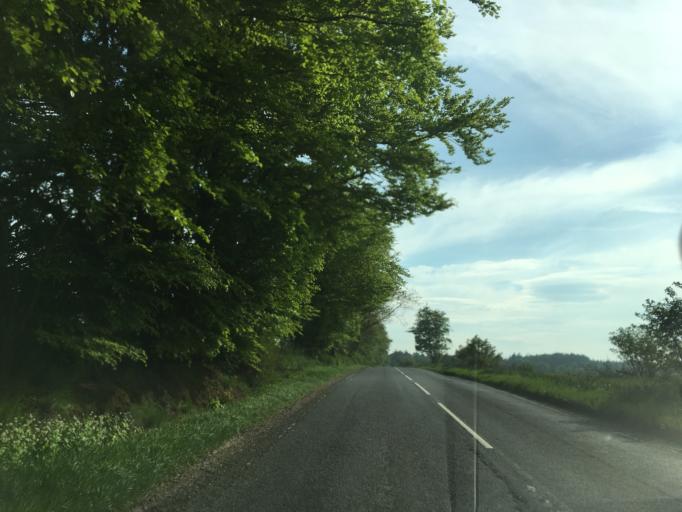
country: GB
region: Scotland
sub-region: Midlothian
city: Penicuik
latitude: 55.7735
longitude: -3.2425
